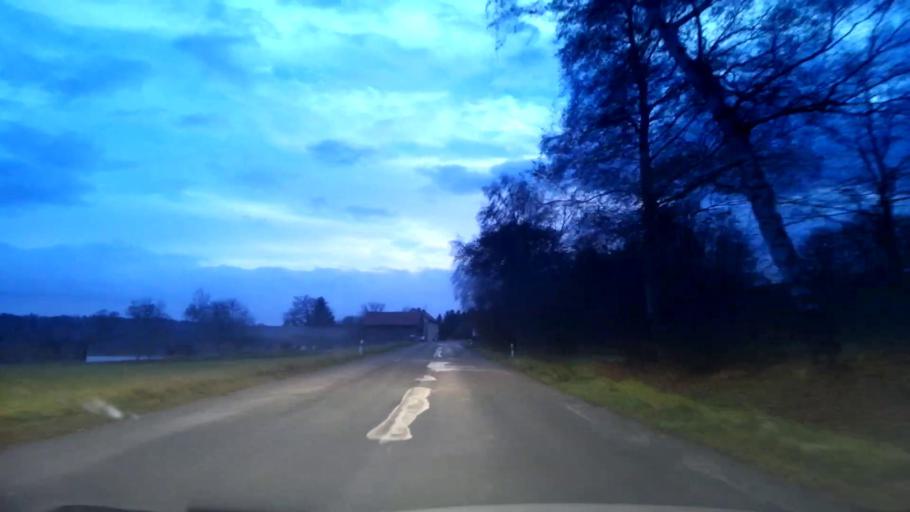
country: DE
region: Bavaria
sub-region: Upper Palatinate
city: Pechbrunn
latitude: 50.0031
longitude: 12.1935
